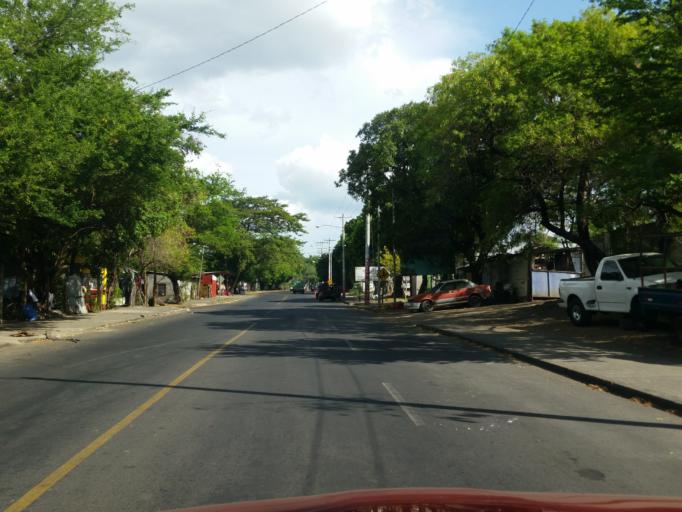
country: NI
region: Managua
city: Managua
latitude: 12.1426
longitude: -86.2682
